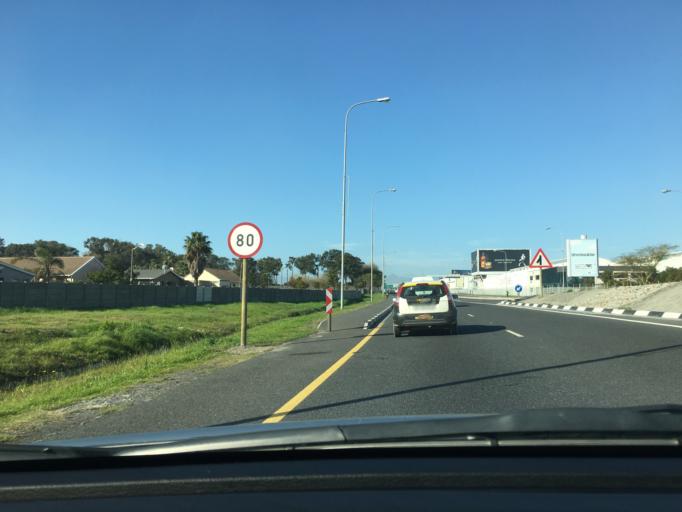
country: ZA
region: Western Cape
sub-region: City of Cape Town
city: Lansdowne
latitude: -33.9674
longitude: 18.5752
